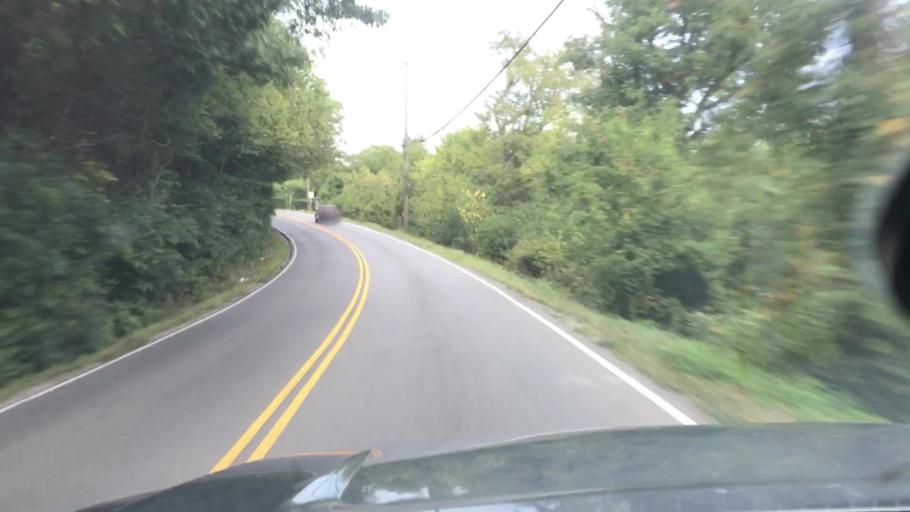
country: US
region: Tennessee
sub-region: Rutherford County
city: La Vergne
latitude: 36.0422
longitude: -86.6366
